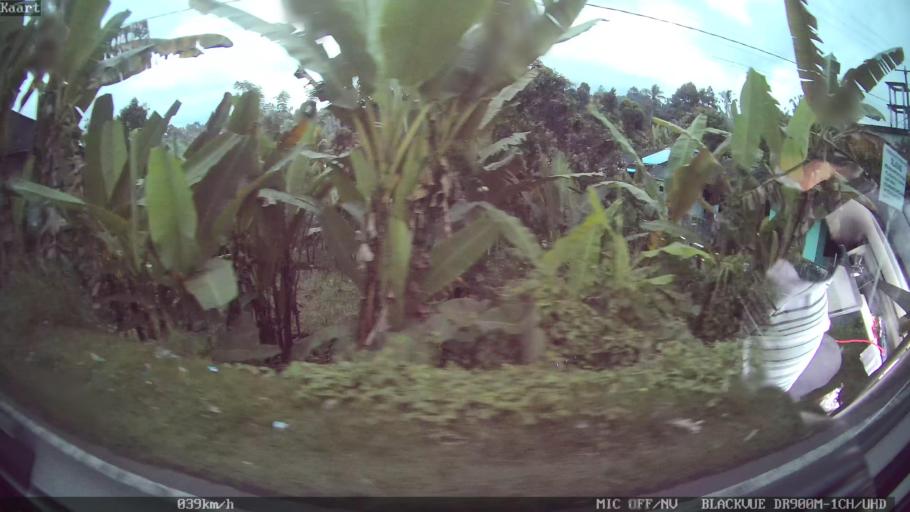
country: ID
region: Bali
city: Petang
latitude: -8.3737
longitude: 115.2239
